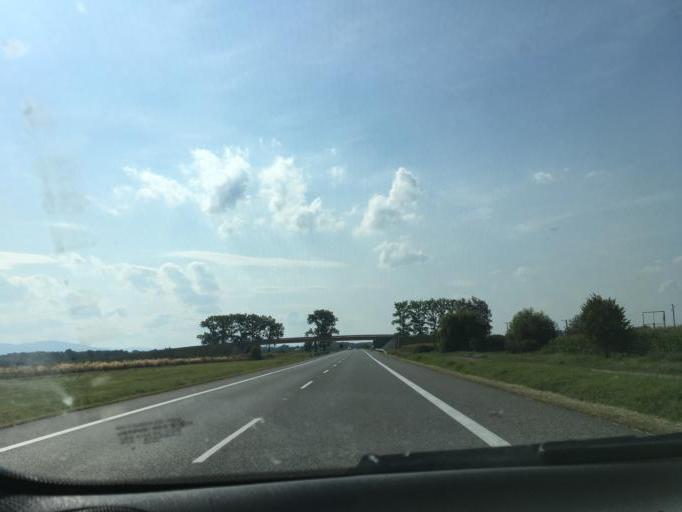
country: PL
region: Opole Voivodeship
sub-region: Powiat prudnicki
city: Lubrza
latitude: 50.3290
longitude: 17.6258
